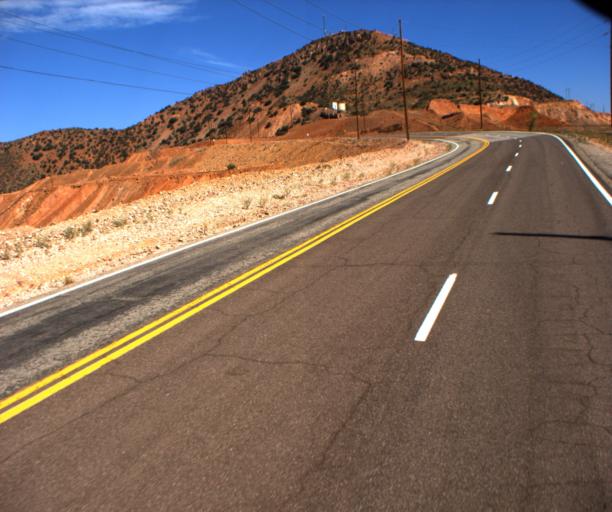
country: US
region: Arizona
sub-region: Greenlee County
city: Morenci
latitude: 33.0843
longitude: -109.3807
